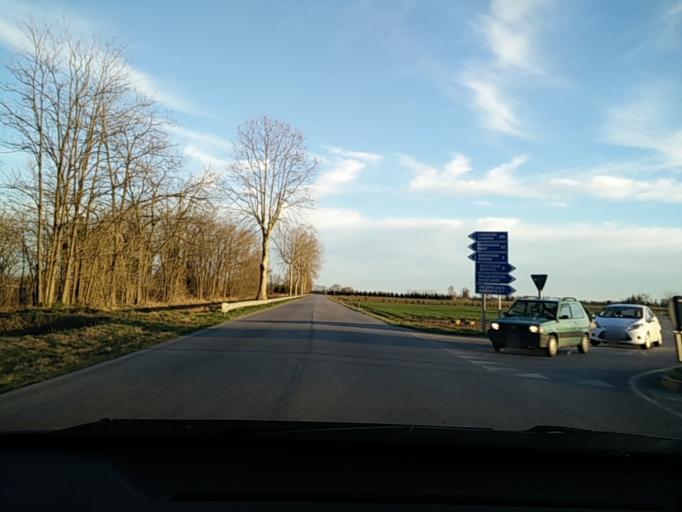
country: IT
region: Friuli Venezia Giulia
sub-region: Provincia di Udine
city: Basiliano-Vissandone
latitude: 46.0018
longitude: 13.1179
